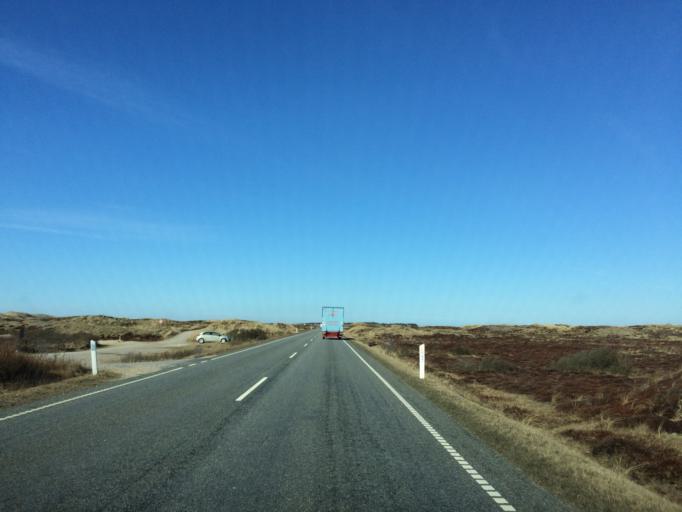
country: DK
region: Central Jutland
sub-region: Ringkobing-Skjern Kommune
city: Hvide Sande
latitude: 55.8341
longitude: 8.1728
